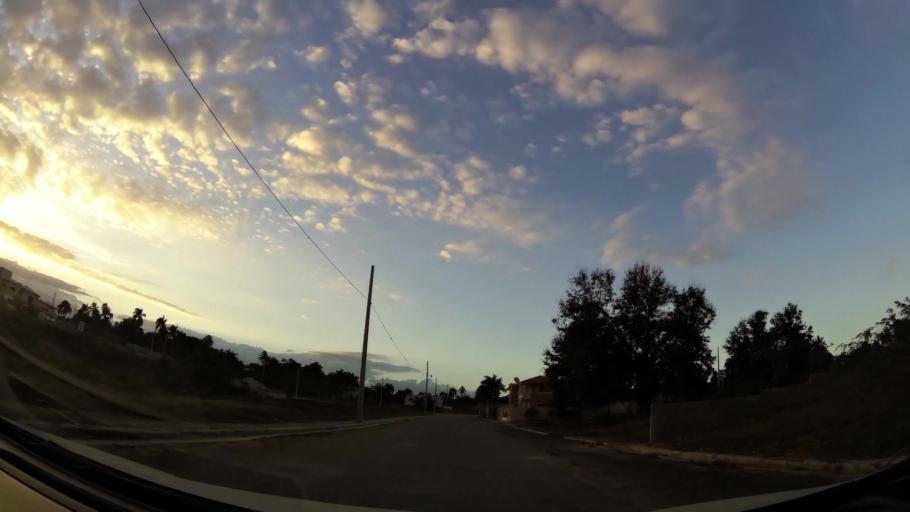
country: DO
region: Nacional
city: La Agustina
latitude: 18.5672
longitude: -69.9390
